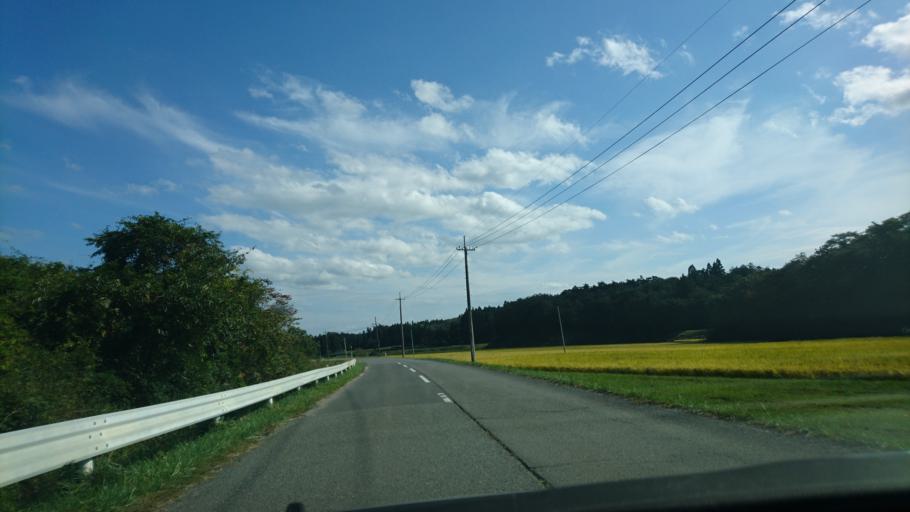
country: JP
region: Iwate
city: Ichinoseki
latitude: 38.8787
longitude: 141.0672
